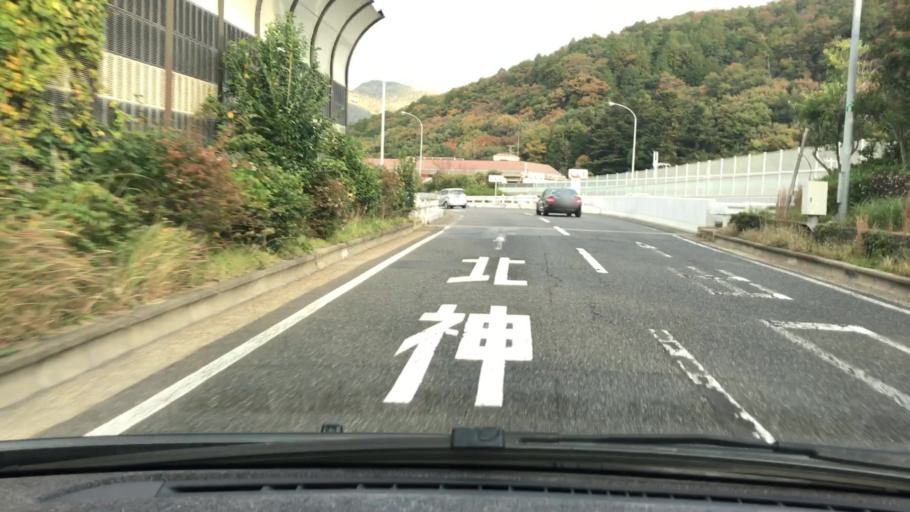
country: JP
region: Hyogo
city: Kobe
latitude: 34.7607
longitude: 135.1588
